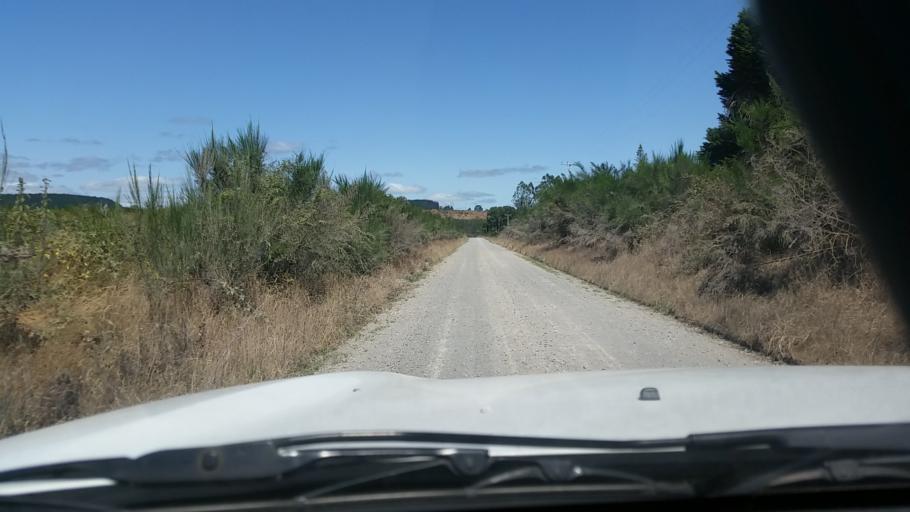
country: NZ
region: Bay of Plenty
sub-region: Whakatane District
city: Murupara
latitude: -38.3346
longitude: 176.5636
